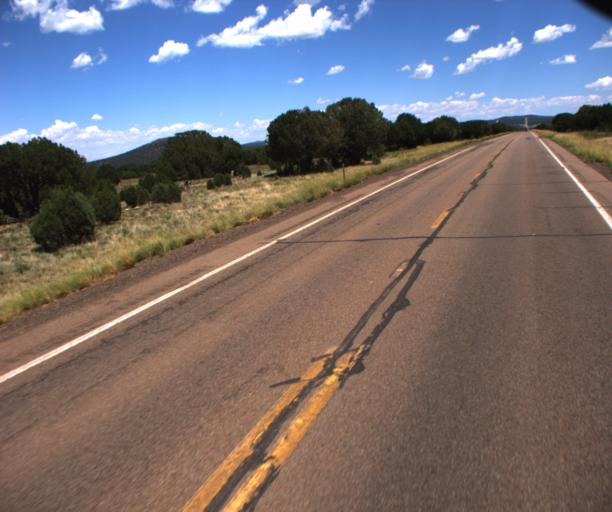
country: US
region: Arizona
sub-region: Navajo County
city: White Mountain Lake
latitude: 34.2759
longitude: -109.8943
